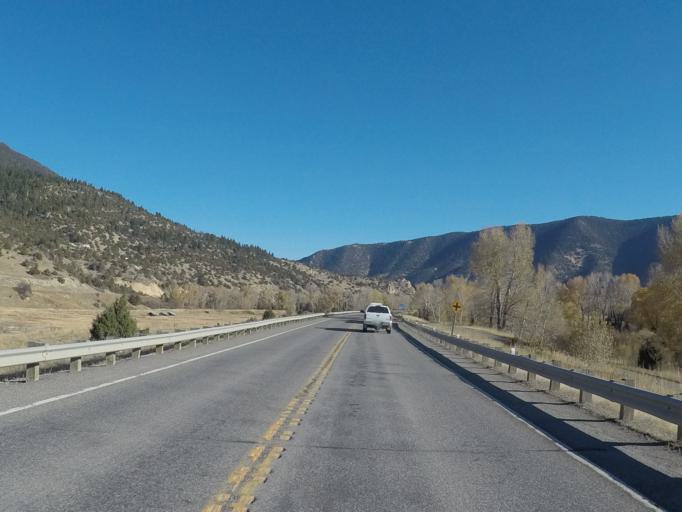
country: US
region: Montana
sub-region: Park County
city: Livingston
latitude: 45.5742
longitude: -110.5870
